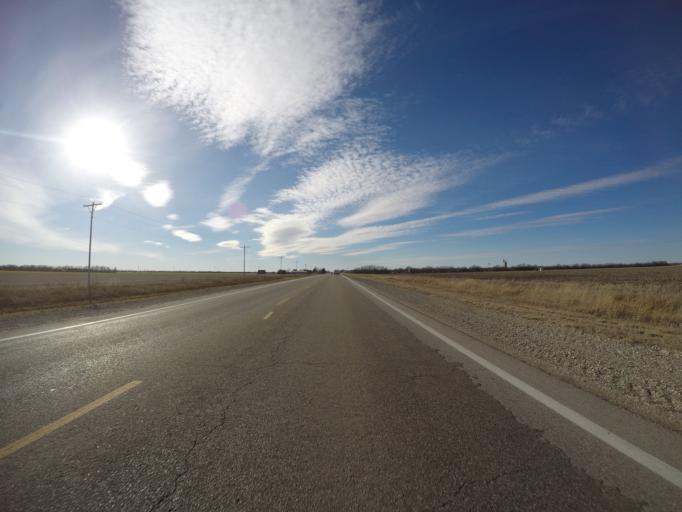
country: US
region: Kansas
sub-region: McPherson County
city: McPherson
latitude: 38.3771
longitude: -97.5230
